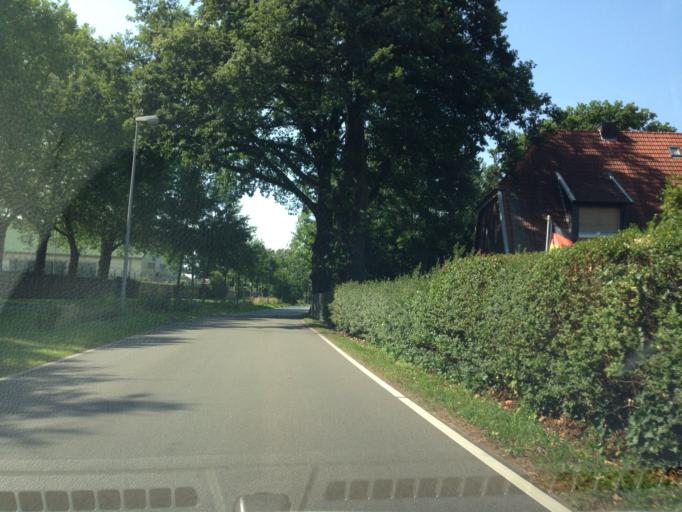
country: DE
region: North Rhine-Westphalia
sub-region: Regierungsbezirk Munster
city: Muenster
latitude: 51.9614
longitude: 7.5779
